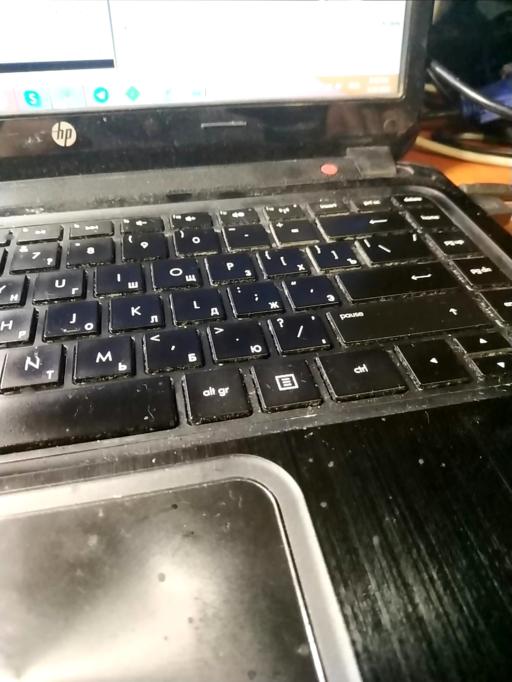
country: RU
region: Tverskaya
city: Spirovo
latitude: 57.4111
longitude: 35.1041
